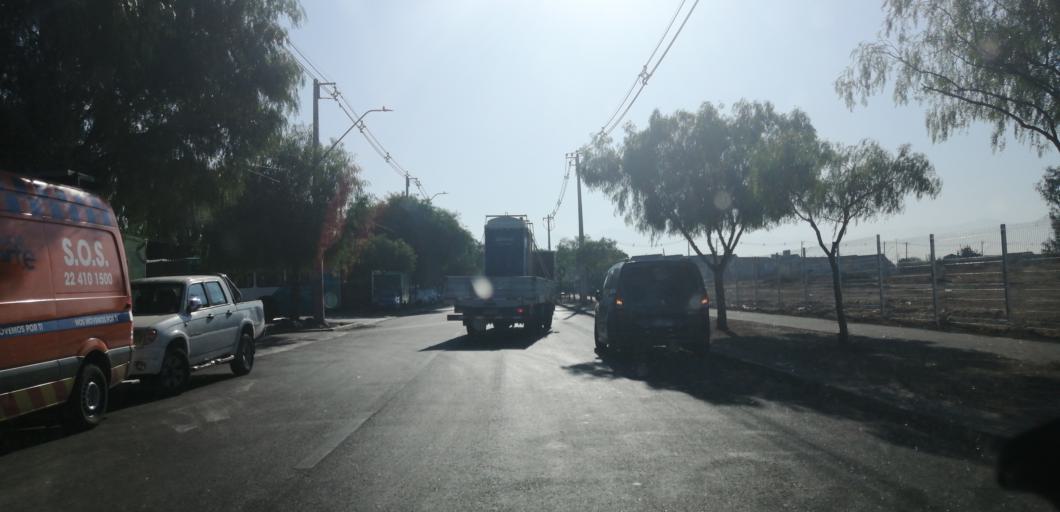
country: CL
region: Santiago Metropolitan
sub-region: Provincia de Santiago
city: Lo Prado
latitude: -33.4350
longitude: -70.7830
